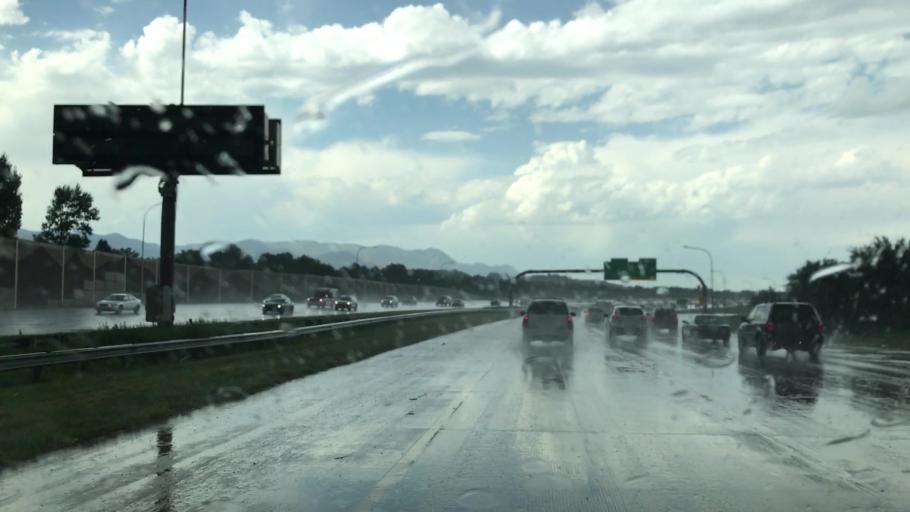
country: US
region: Colorado
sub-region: El Paso County
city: Colorado Springs
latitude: 38.8559
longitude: -104.8332
